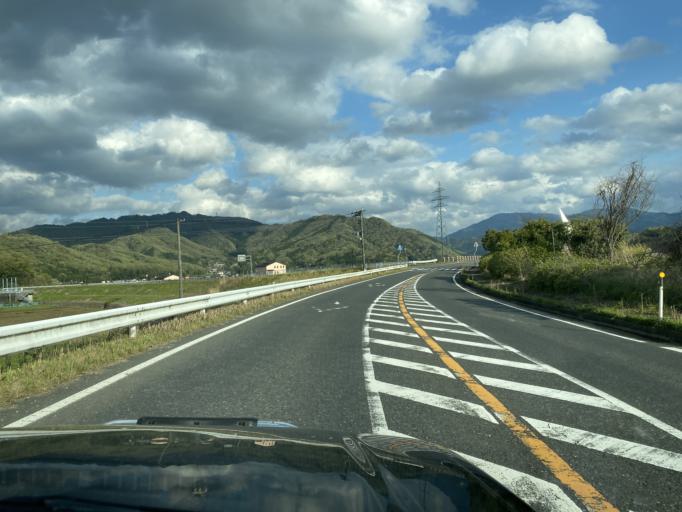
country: JP
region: Hyogo
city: Toyooka
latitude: 35.4881
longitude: 134.8557
